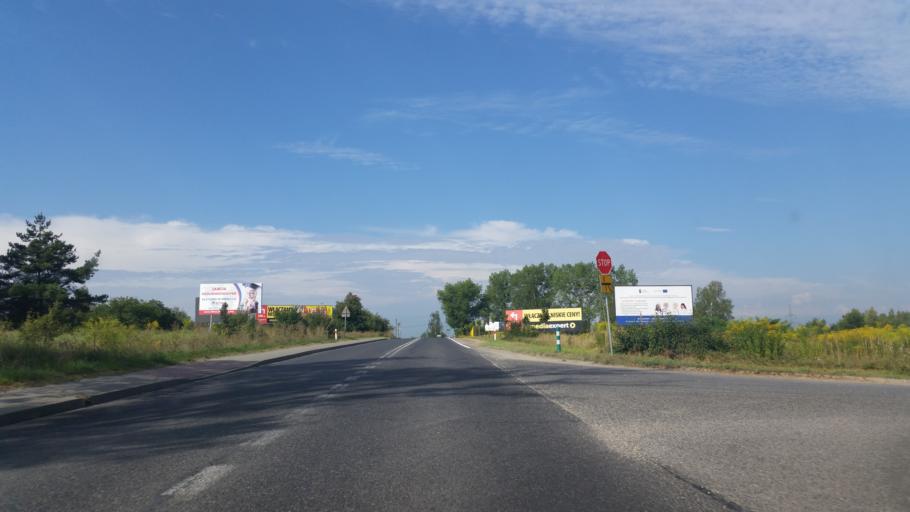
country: PL
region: Lesser Poland Voivodeship
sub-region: Powiat chrzanowski
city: Libiaz
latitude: 50.1110
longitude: 19.3421
